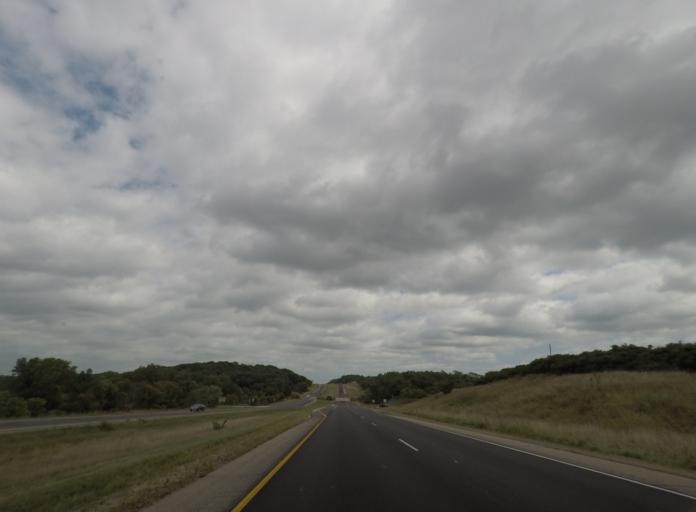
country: US
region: Iowa
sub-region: Linn County
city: Ely
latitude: 41.9254
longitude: -91.5815
